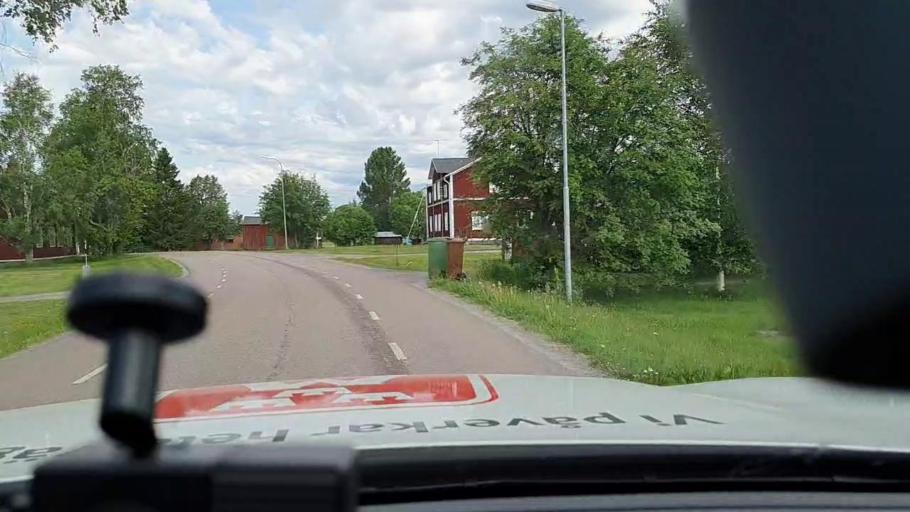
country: SE
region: Norrbotten
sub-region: Bodens Kommun
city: Saevast
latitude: 65.6835
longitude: 21.7978
